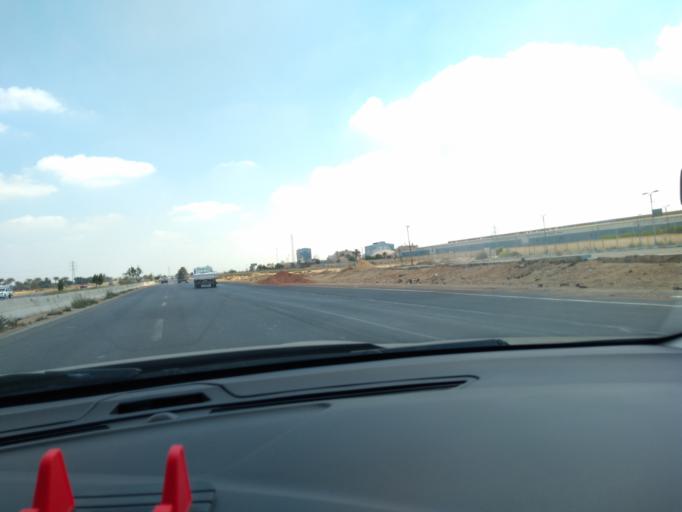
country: EG
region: Al Isma'iliyah
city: At Tall al Kabir
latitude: 30.3389
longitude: 31.8634
